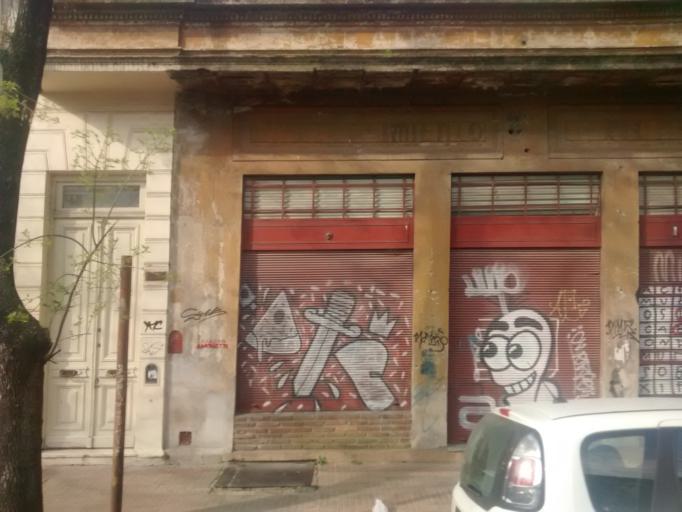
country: AR
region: Buenos Aires
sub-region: Partido de La Plata
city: La Plata
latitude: -34.9229
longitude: -57.9457
